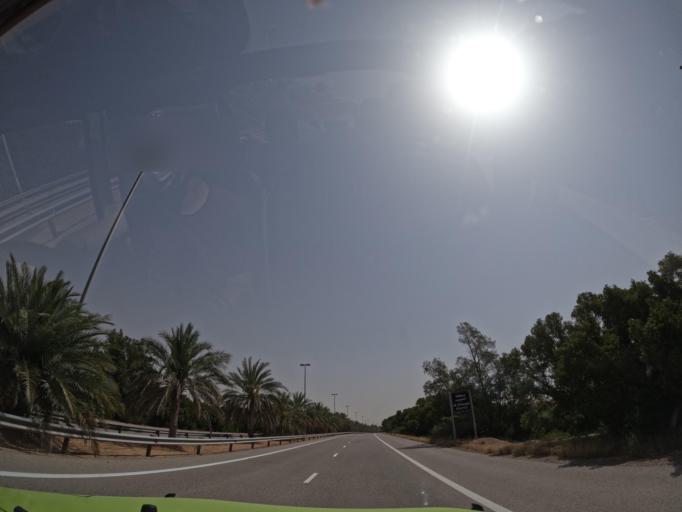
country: OM
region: Al Buraimi
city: Al Buraymi
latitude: 24.6919
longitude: 55.7305
